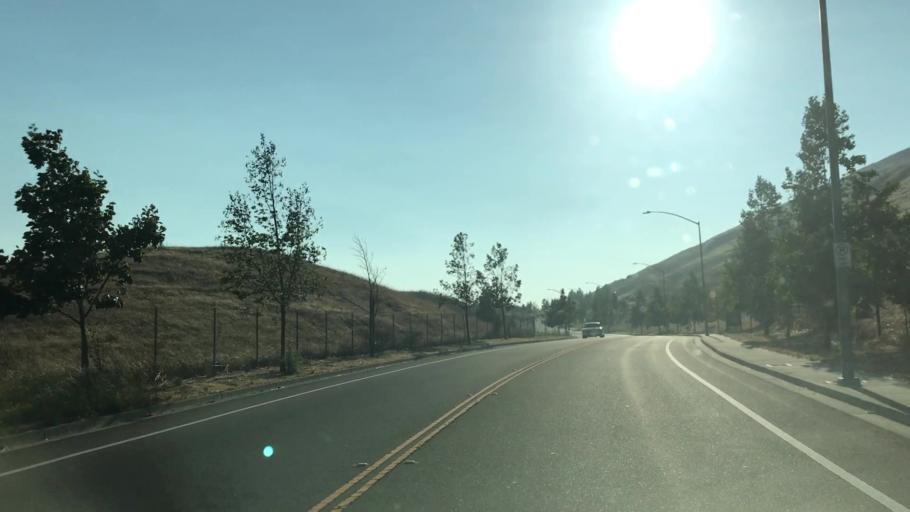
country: US
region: California
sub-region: Alameda County
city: Dublin
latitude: 37.6988
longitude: -121.9614
